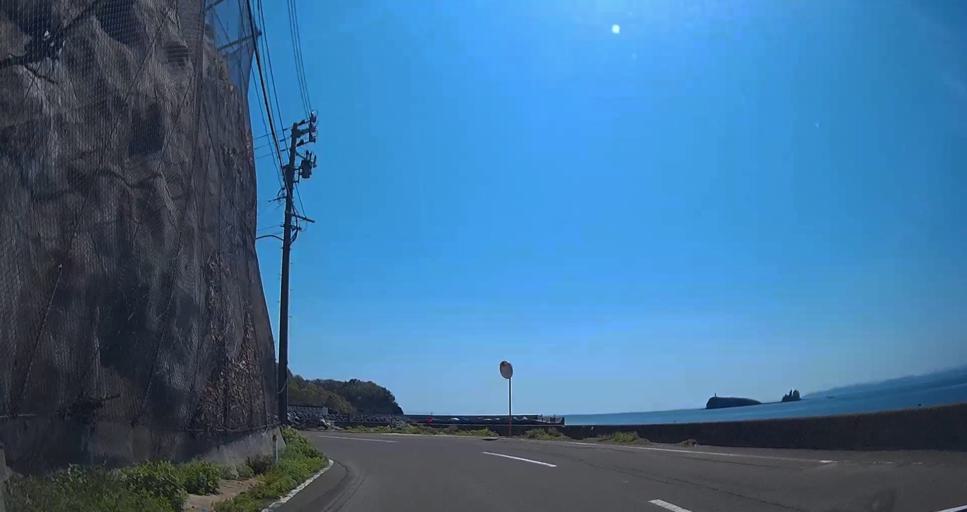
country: JP
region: Aomori
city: Aomori Shi
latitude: 41.1287
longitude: 140.8038
